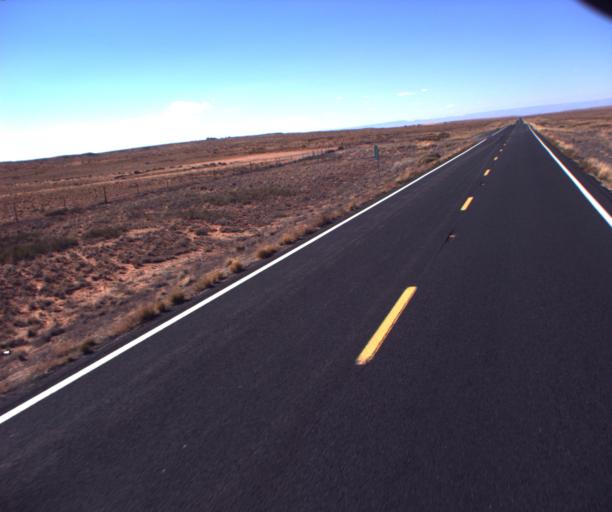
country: US
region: Arizona
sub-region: Coconino County
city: Tuba City
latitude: 36.0140
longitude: -111.0867
